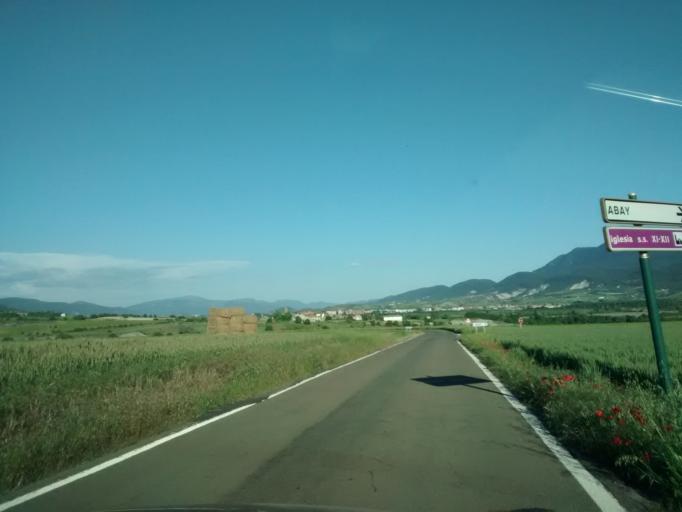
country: ES
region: Aragon
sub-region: Provincia de Huesca
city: Jaca
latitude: 42.5833
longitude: -0.5969
